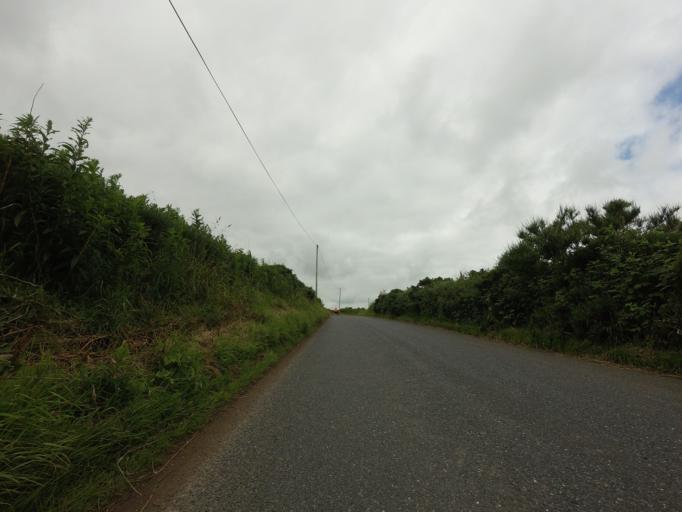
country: GB
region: Scotland
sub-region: Aberdeenshire
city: Rosehearty
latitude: 57.5405
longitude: -2.1987
